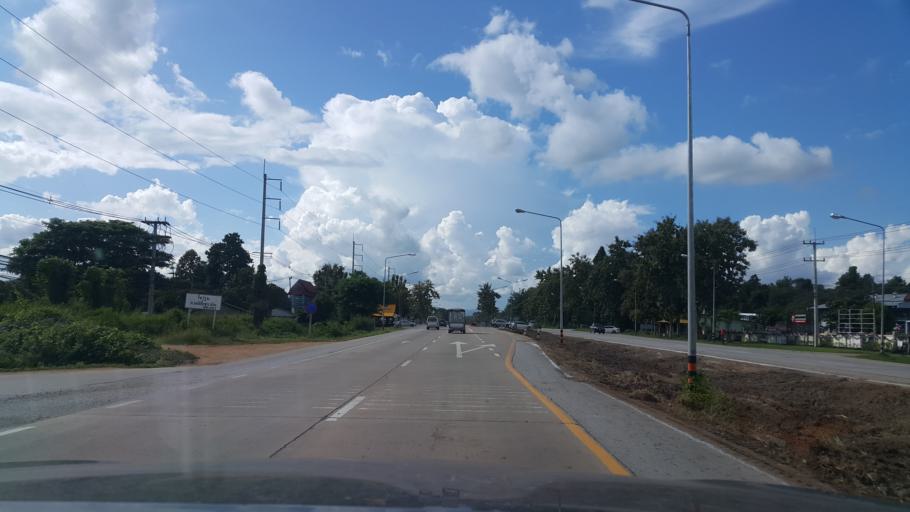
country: TH
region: Lampang
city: Hang Chat
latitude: 18.2961
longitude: 99.4154
